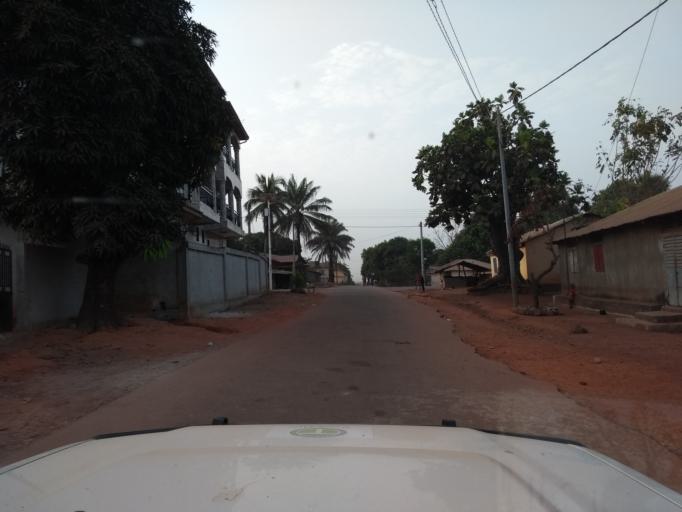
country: GN
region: Kindia
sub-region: Prefecture de Dubreka
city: Dubreka
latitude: 9.7892
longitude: -13.5229
